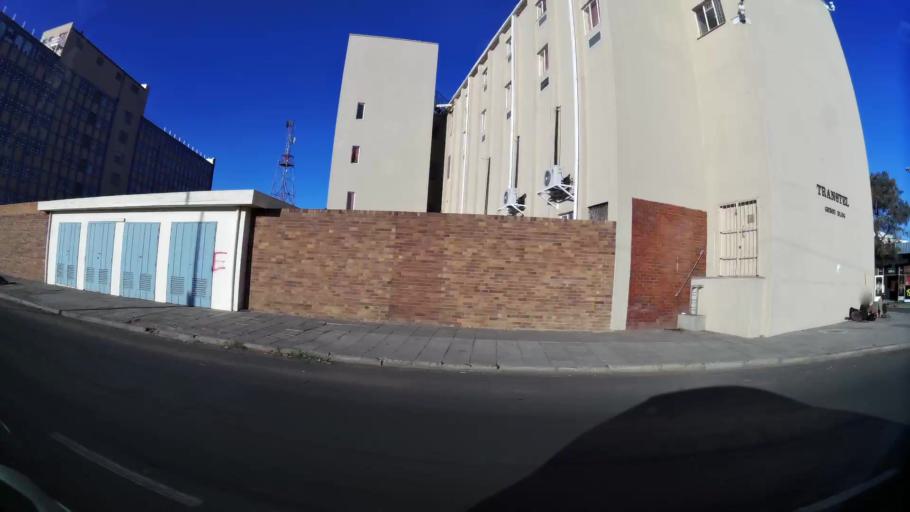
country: ZA
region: Northern Cape
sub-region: Frances Baard District Municipality
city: Kimberley
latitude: -28.7368
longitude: 24.7686
